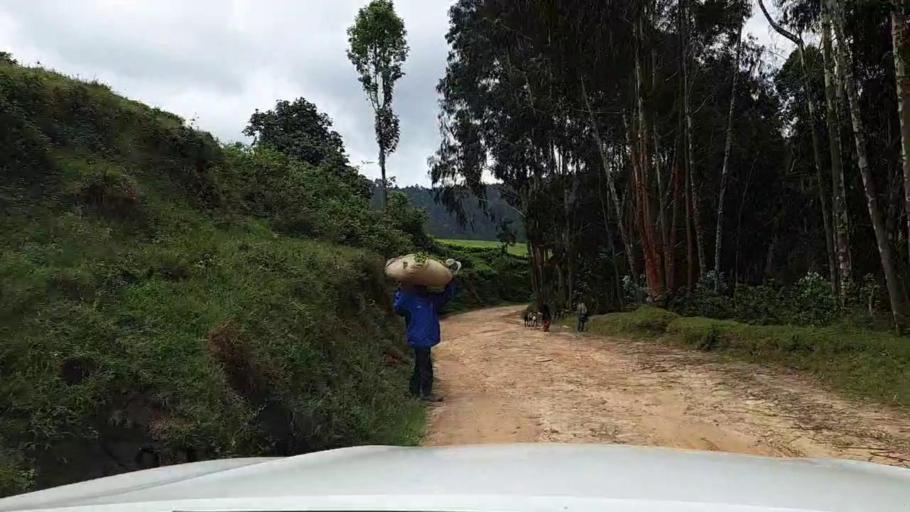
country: RW
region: Western Province
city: Kibuye
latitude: -2.2783
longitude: 29.3659
